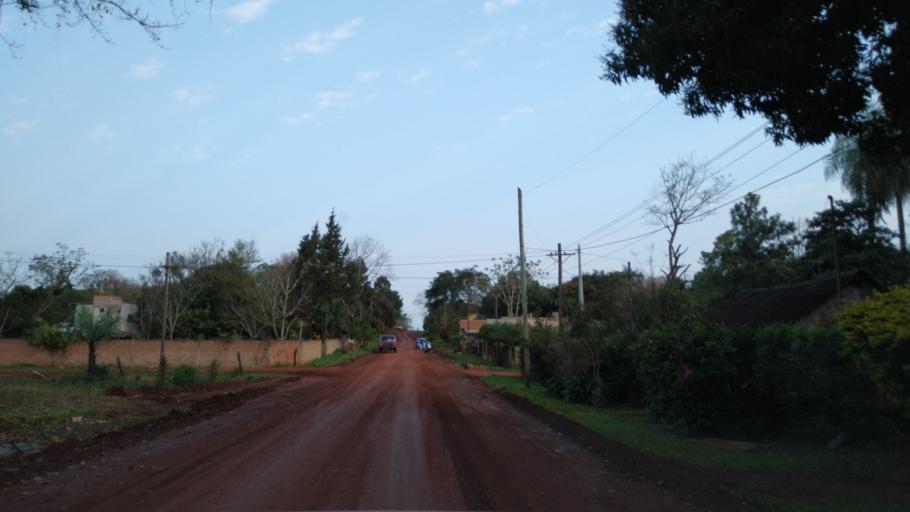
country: AR
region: Corrientes
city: San Carlos
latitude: -27.7461
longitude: -55.9012
